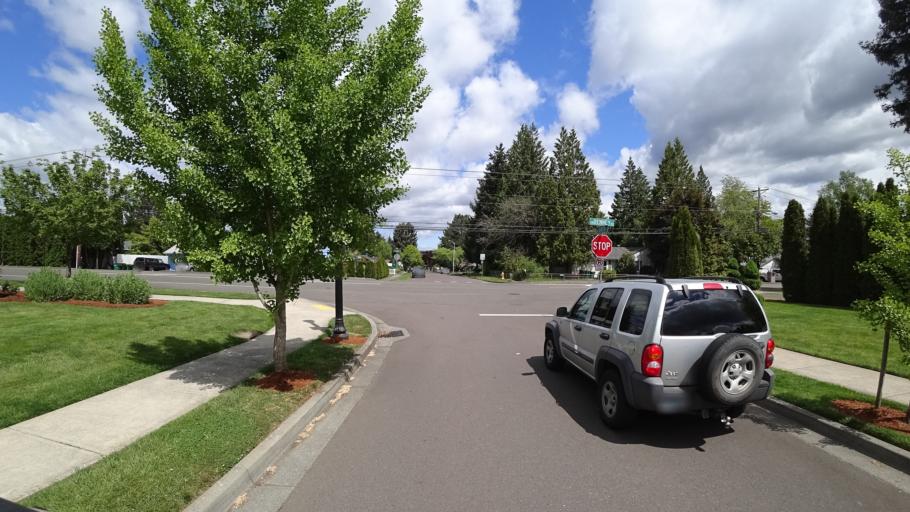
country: US
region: Oregon
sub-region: Washington County
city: Beaverton
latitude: 45.4691
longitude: -122.7957
